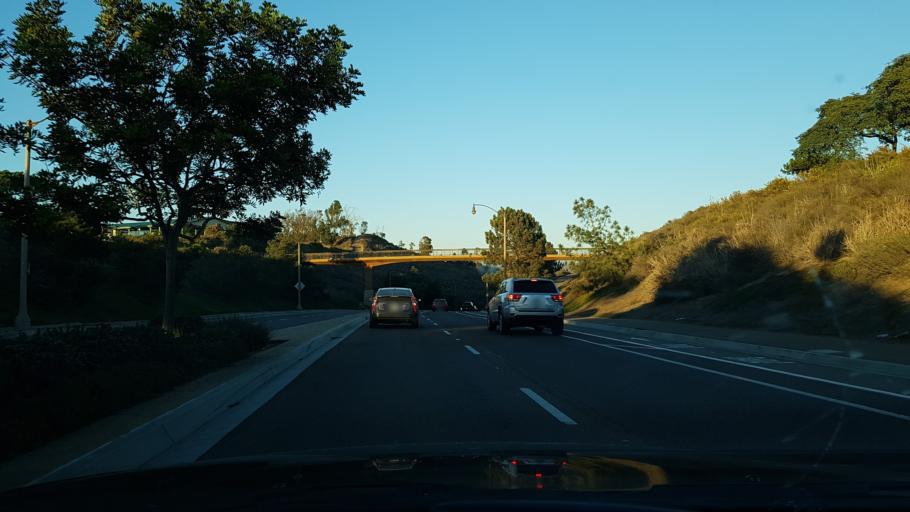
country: US
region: California
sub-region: San Diego County
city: Encinitas
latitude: 33.0669
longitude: -117.2753
